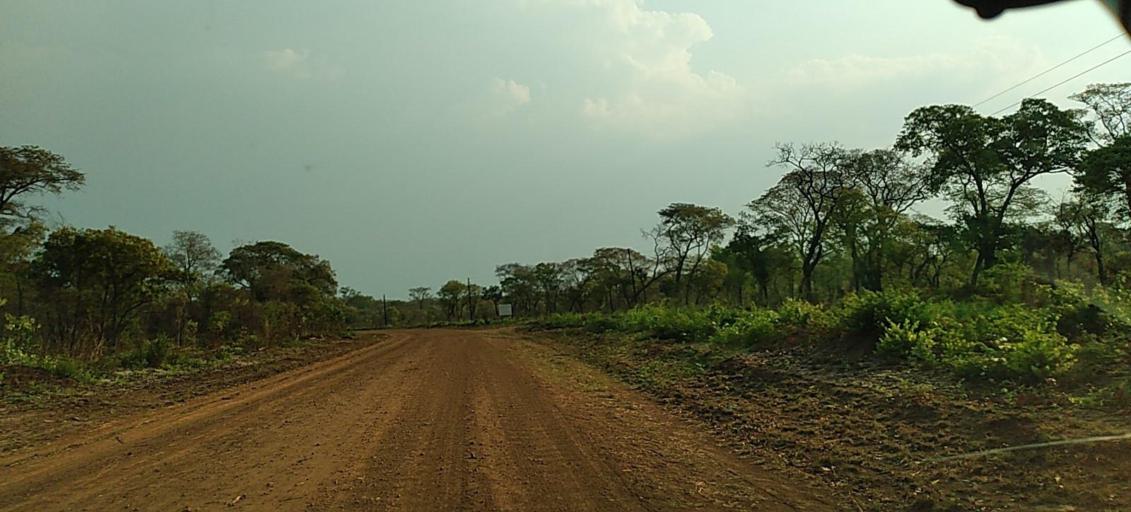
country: ZM
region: Western
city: Lukulu
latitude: -13.9929
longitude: 23.6158
